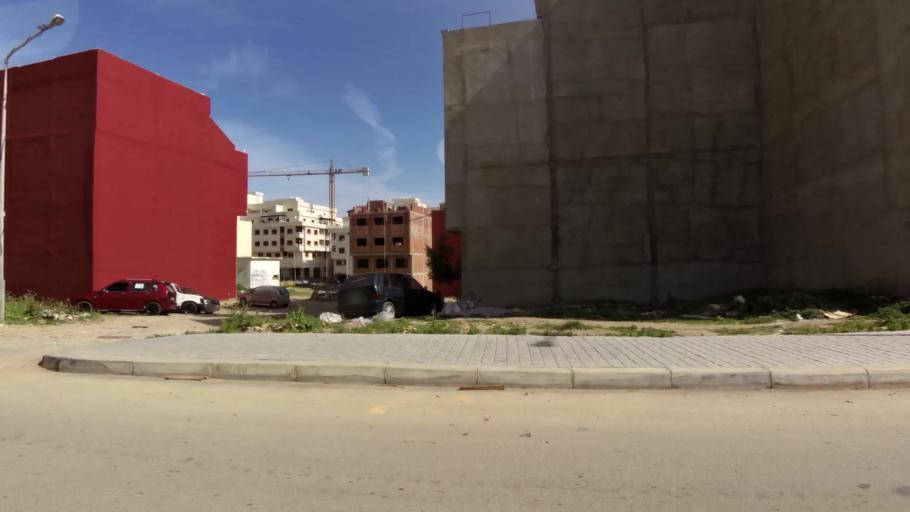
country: MA
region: Tanger-Tetouan
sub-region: Tanger-Assilah
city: Tangier
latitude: 35.7273
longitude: -5.8089
